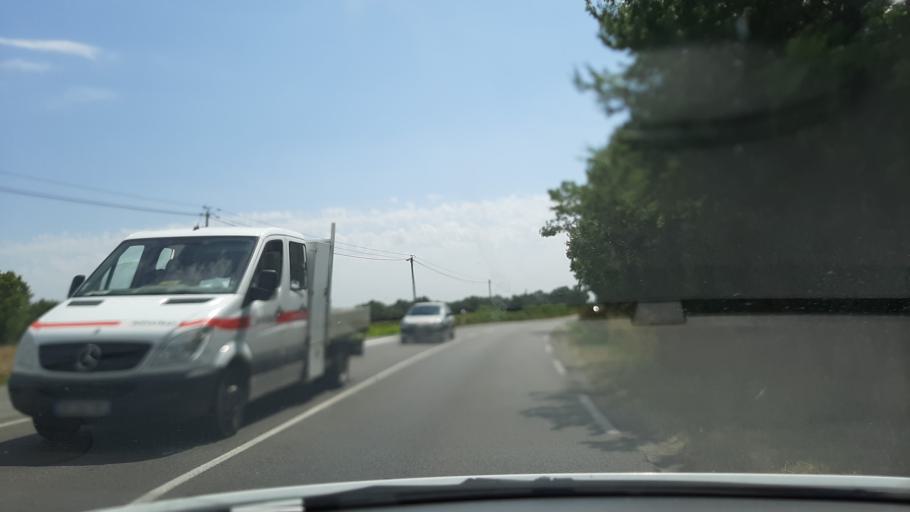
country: FR
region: Pays de la Loire
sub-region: Departement de la Vendee
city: Le Poire-sur-Vie
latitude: 46.7624
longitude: -1.4864
